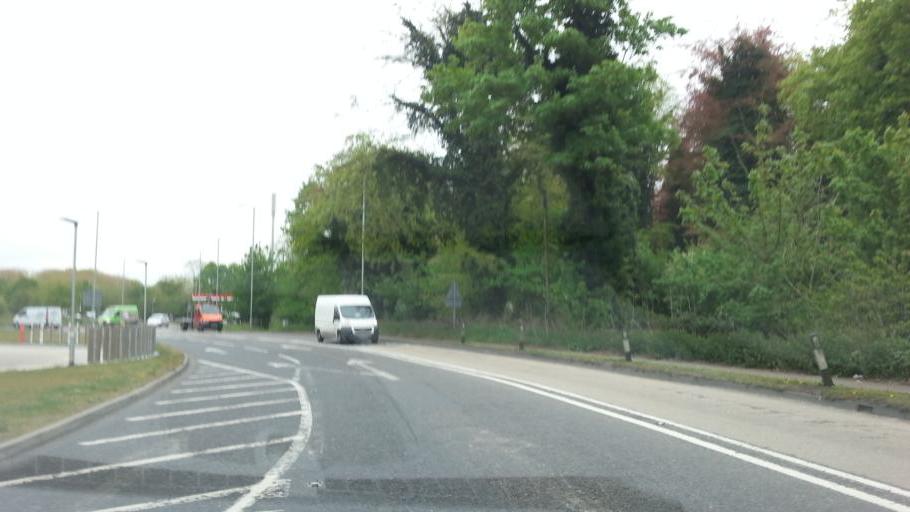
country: GB
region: England
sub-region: Suffolk
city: Lakenheath
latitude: 52.3384
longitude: 0.5331
